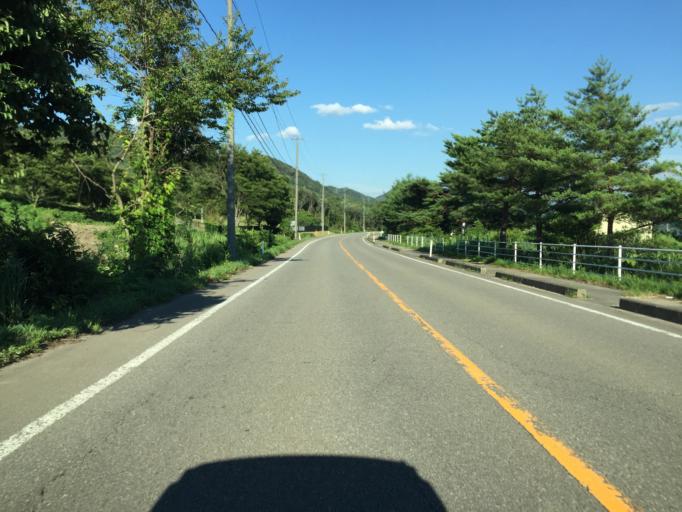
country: JP
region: Miyagi
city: Shiroishi
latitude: 37.9846
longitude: 140.4622
